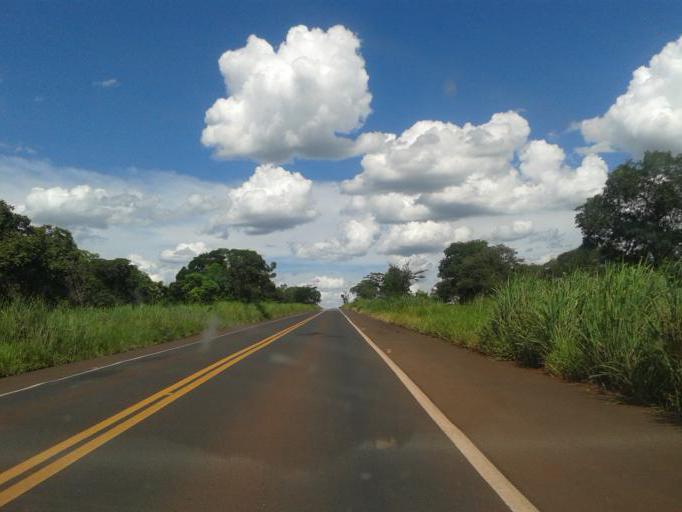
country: BR
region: Minas Gerais
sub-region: Santa Vitoria
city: Santa Vitoria
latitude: -18.8758
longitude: -50.1066
